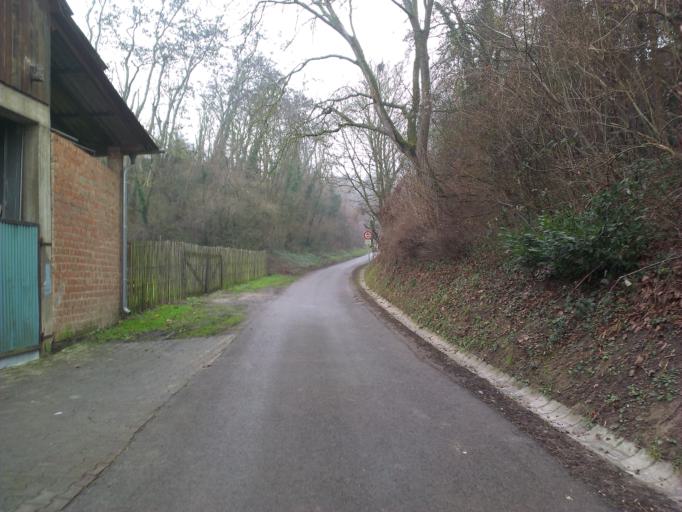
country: DE
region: Baden-Wuerttemberg
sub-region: Karlsruhe Region
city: Ubstadt-Weiher
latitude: 49.1479
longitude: 8.6689
